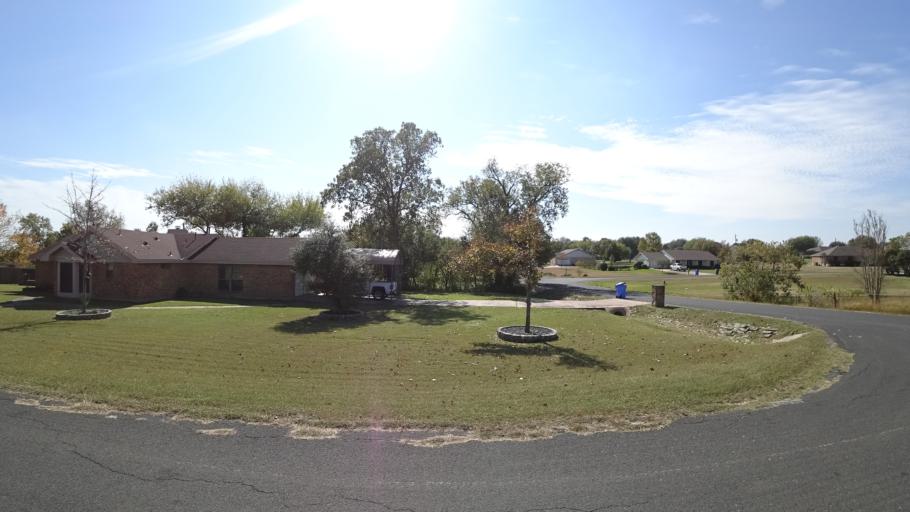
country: US
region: Texas
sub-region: Travis County
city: Pflugerville
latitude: 30.4132
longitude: -97.6268
